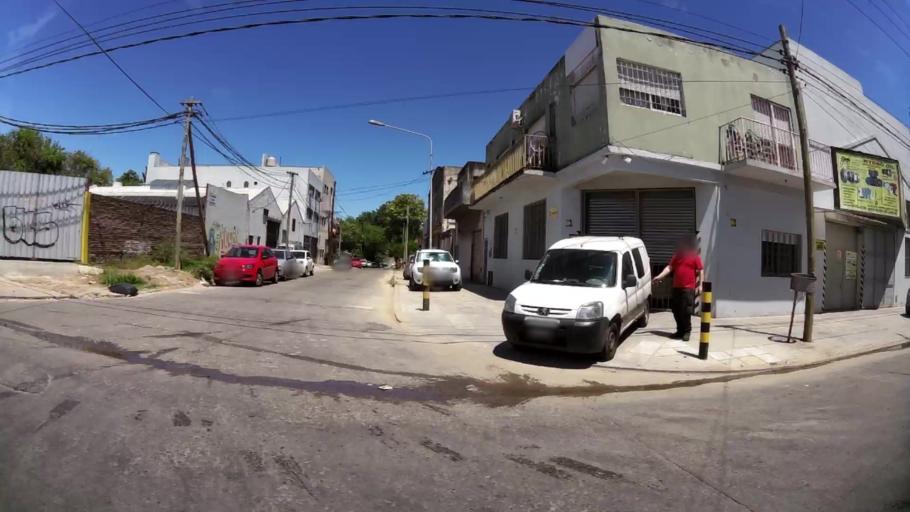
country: AR
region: Buenos Aires
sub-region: Partido de General San Martin
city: General San Martin
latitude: -34.5630
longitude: -58.5153
